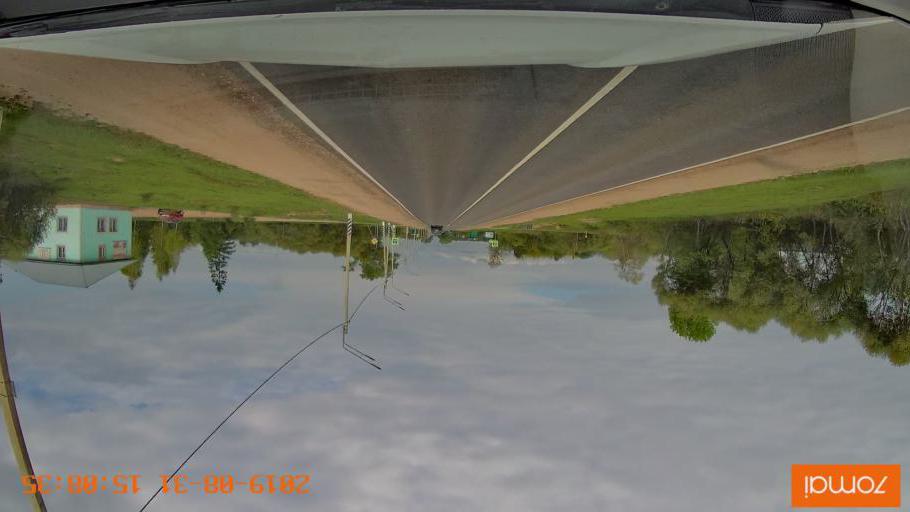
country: RU
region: Kaluga
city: Spas-Demensk
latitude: 54.3937
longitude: 34.1870
